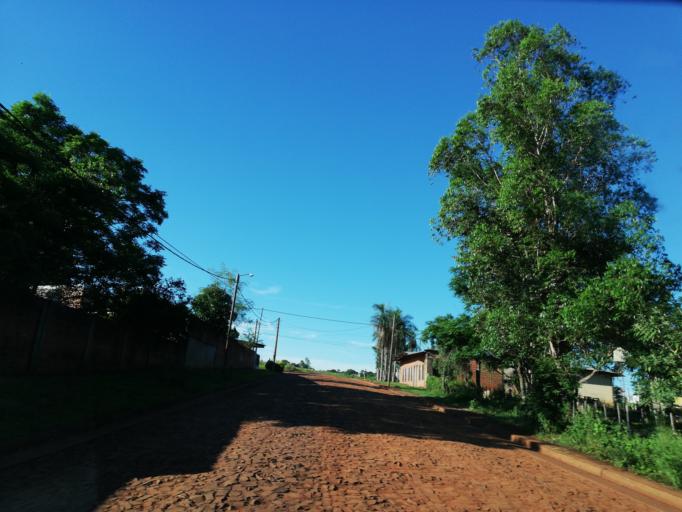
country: AR
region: Misiones
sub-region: Departamento de Capital
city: Posadas
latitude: -27.4345
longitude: -55.9353
